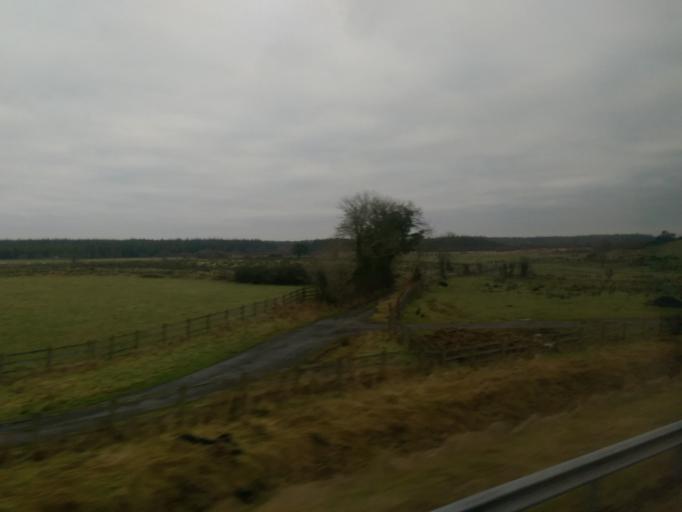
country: IE
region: Connaught
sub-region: County Galway
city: Loughrea
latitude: 53.2847
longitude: -8.4578
